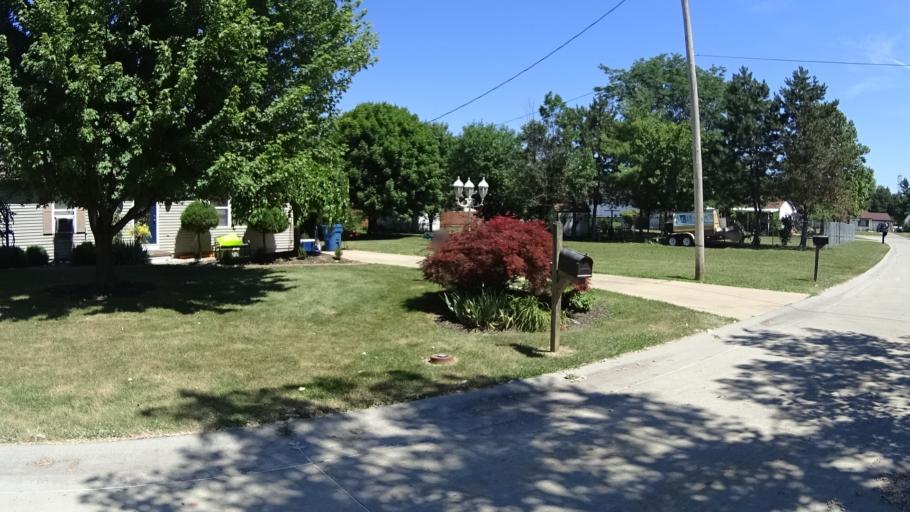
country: US
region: Ohio
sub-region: Erie County
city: Sandusky
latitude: 41.4092
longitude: -82.6935
